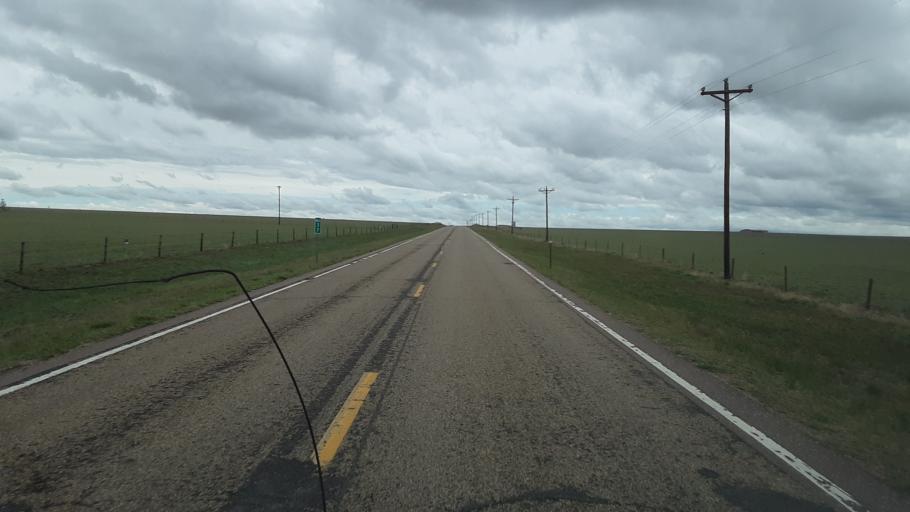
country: US
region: Colorado
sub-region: El Paso County
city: Ellicott
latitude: 38.8399
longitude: -104.0173
